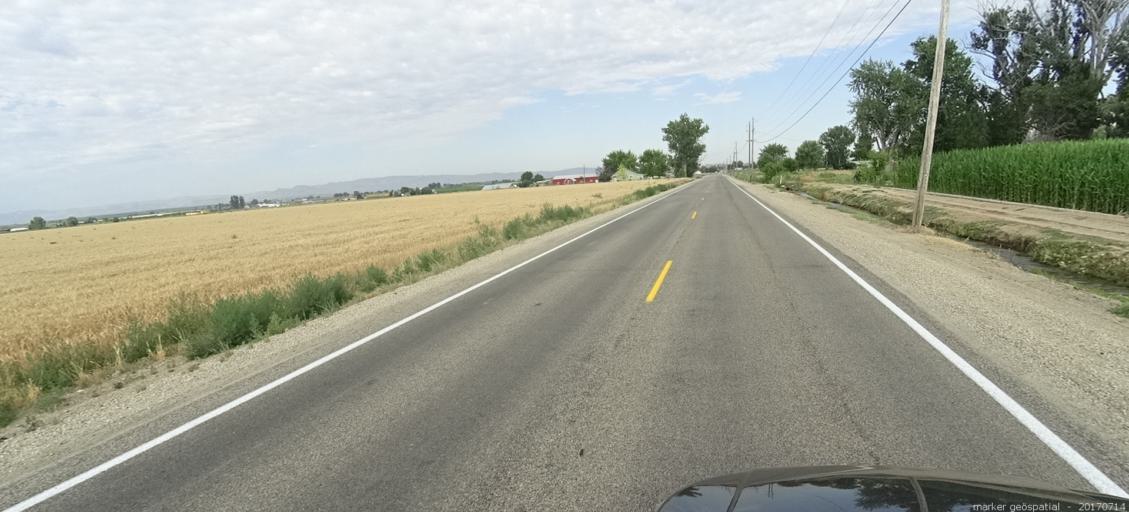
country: US
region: Idaho
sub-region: Ada County
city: Kuna
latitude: 43.4883
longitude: -116.4661
